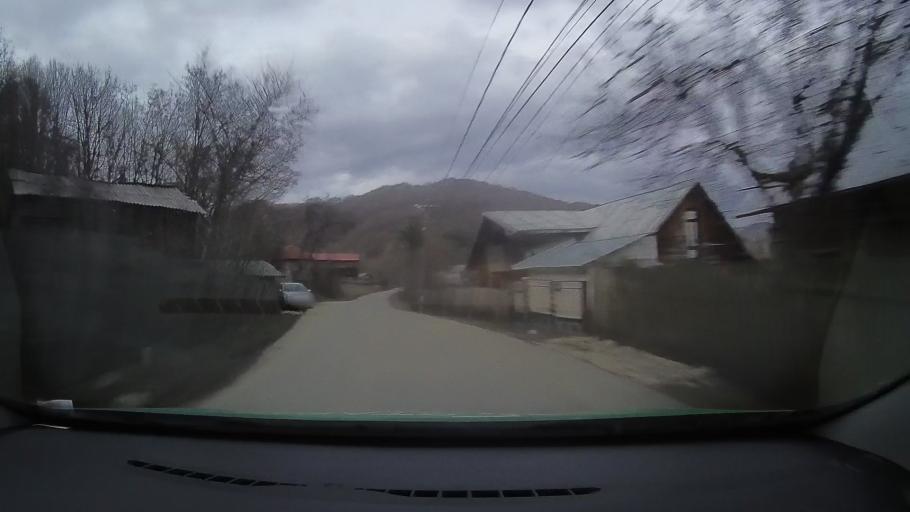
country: RO
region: Prahova
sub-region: Comuna Adunati
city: Adunati
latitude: 45.1149
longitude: 25.5874
